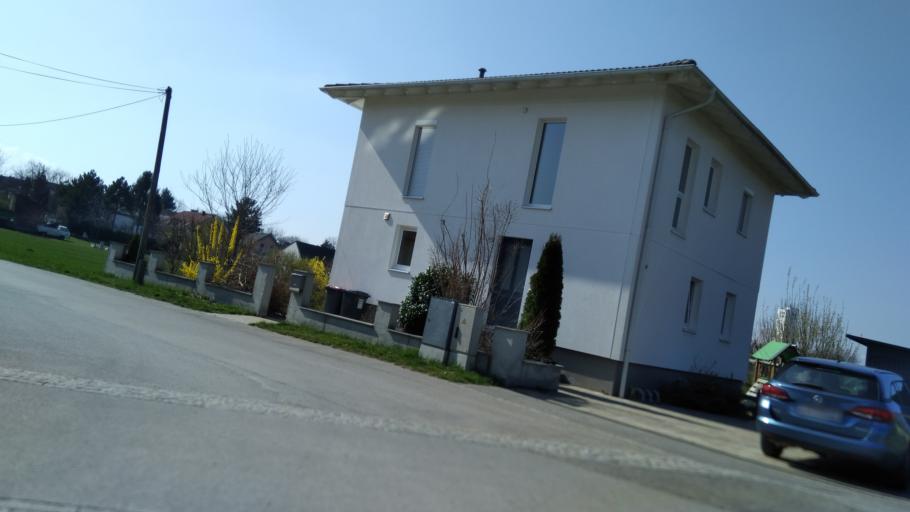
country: AT
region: Lower Austria
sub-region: Politischer Bezirk Mistelbach
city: Wolkersdorf im Weinviertel
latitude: 48.3742
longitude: 16.5248
